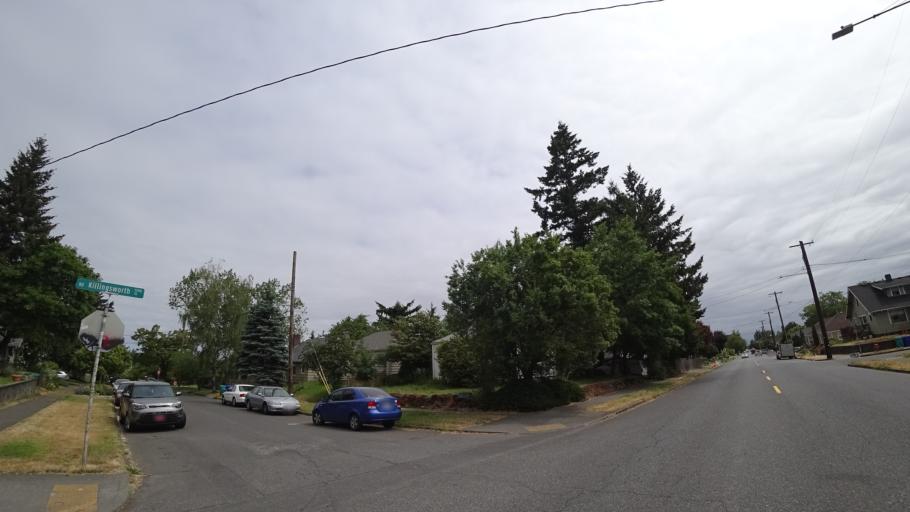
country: US
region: Oregon
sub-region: Multnomah County
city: Portland
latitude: 45.5627
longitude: -122.6415
